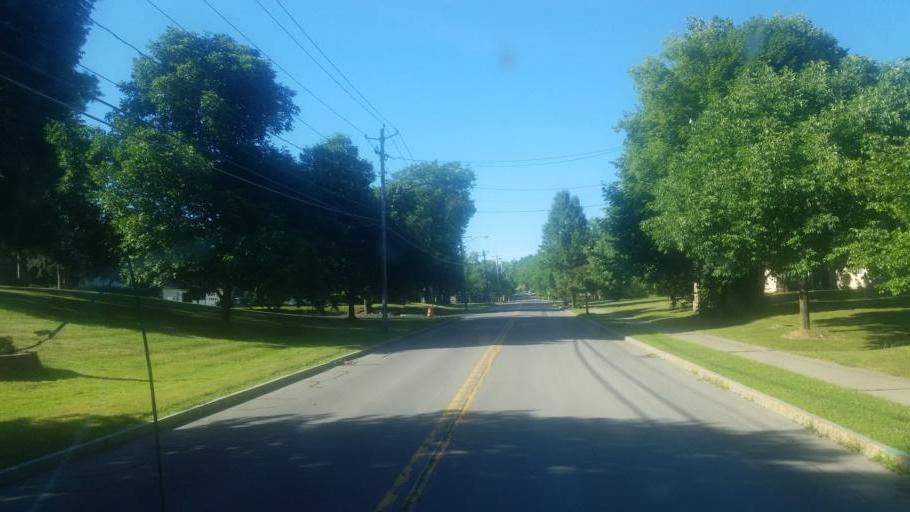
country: US
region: New York
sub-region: Wayne County
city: Newark
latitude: 43.0358
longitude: -77.0965
